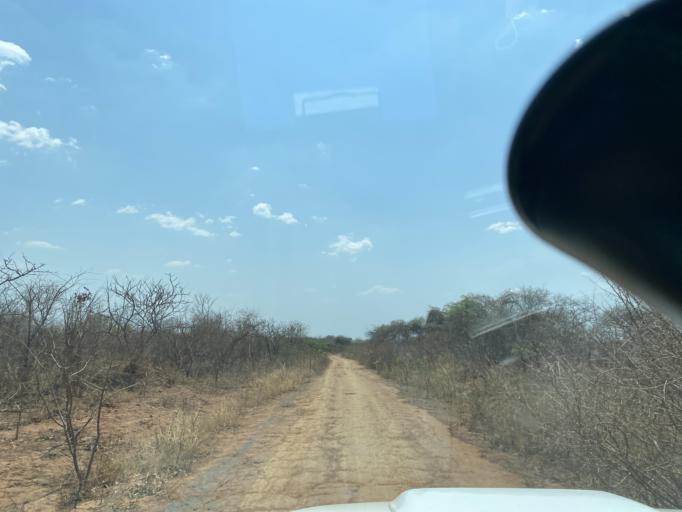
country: ZM
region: Lusaka
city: Lusaka
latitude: -15.5057
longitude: 27.9716
